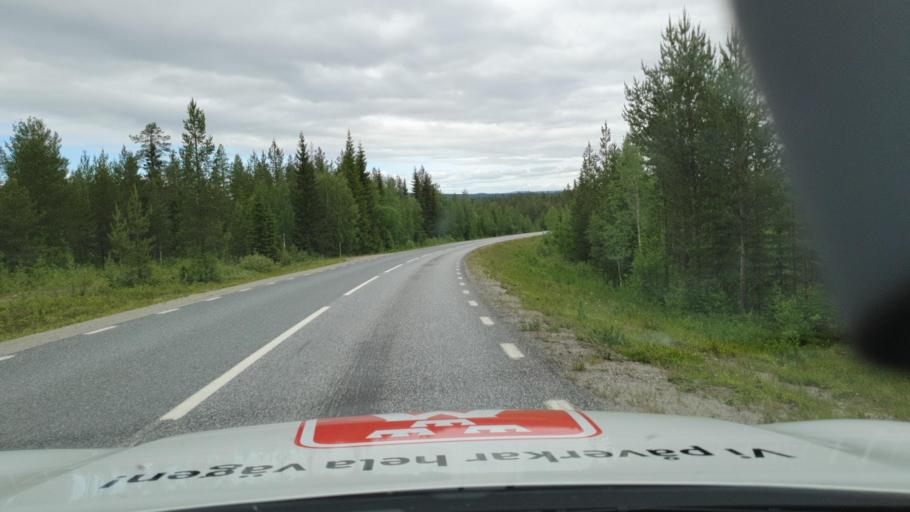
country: SE
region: Vaesterbotten
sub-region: Asele Kommun
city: Asele
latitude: 64.2062
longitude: 17.5108
